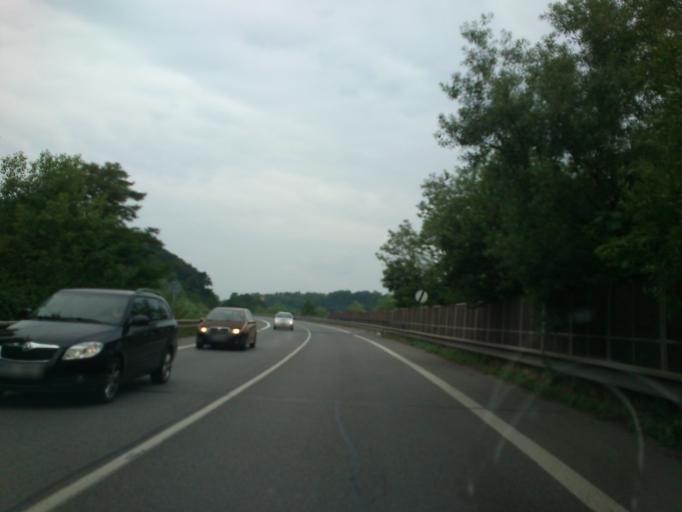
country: CZ
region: Central Bohemia
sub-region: Okres Mlada Boleslav
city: Mlada Boleslav
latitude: 50.4411
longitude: 14.8890
